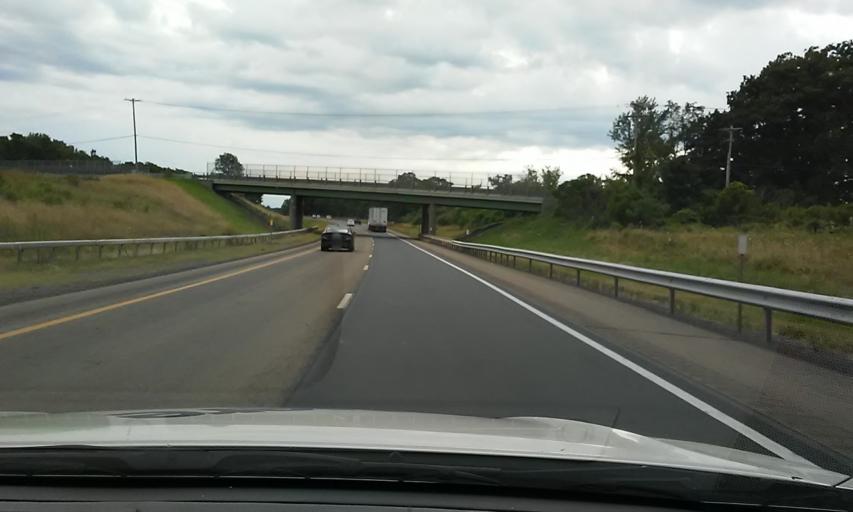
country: US
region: New York
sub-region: Chautauqua County
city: Brocton
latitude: 42.4091
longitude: -79.4403
